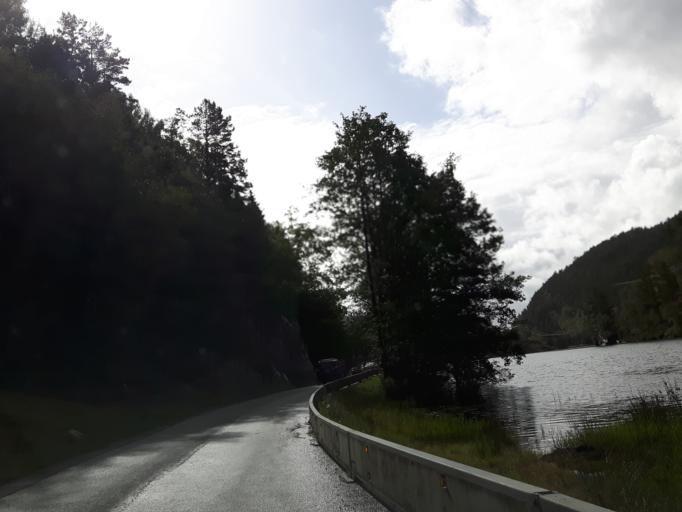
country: NO
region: Rogaland
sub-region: Lund
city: Moi
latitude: 58.3920
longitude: 6.6255
